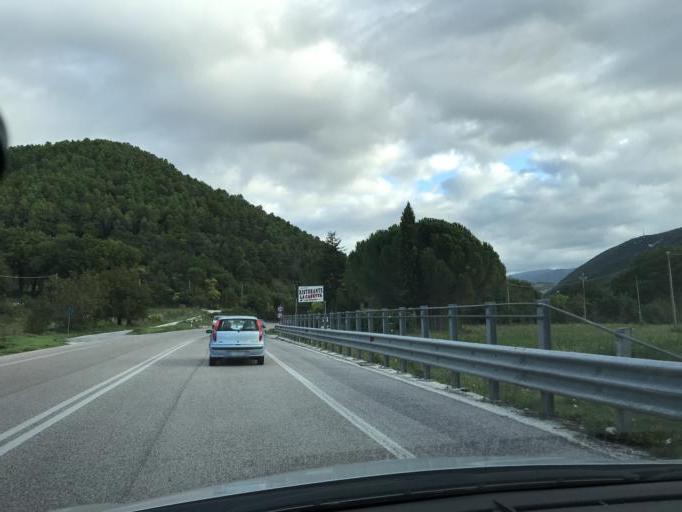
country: IT
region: Umbria
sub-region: Provincia di Perugia
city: Spoleto
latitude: 42.7110
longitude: 12.7196
